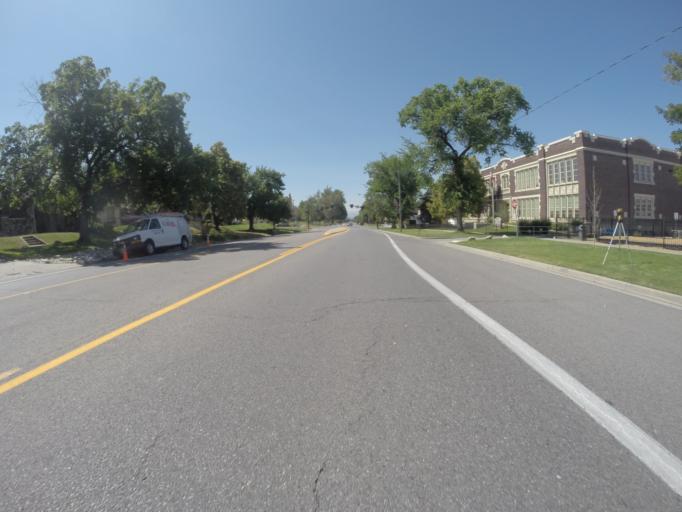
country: US
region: Utah
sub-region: Salt Lake County
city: Salt Lake City
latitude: 40.7552
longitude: -111.8539
